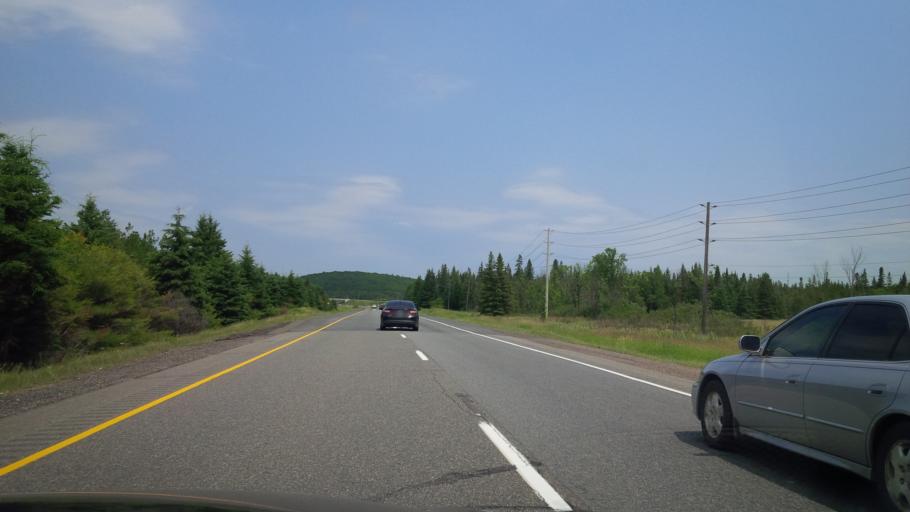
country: CA
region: Ontario
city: Huntsville
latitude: 45.3622
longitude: -79.2186
